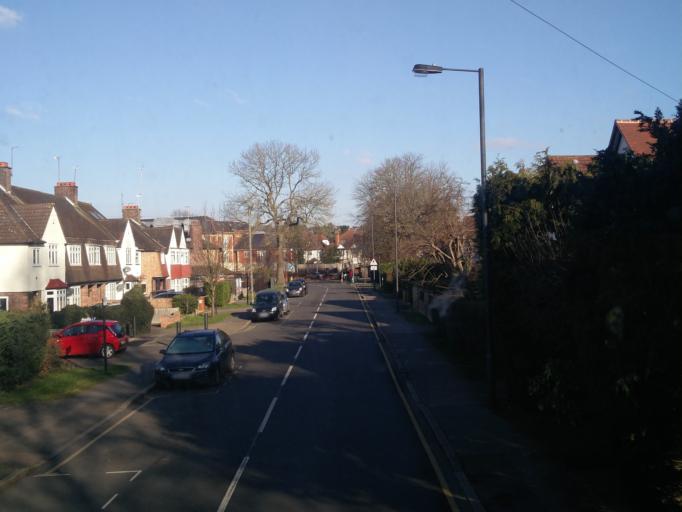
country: GB
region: England
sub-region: Greater London
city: Pinner
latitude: 51.5876
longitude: -0.3819
